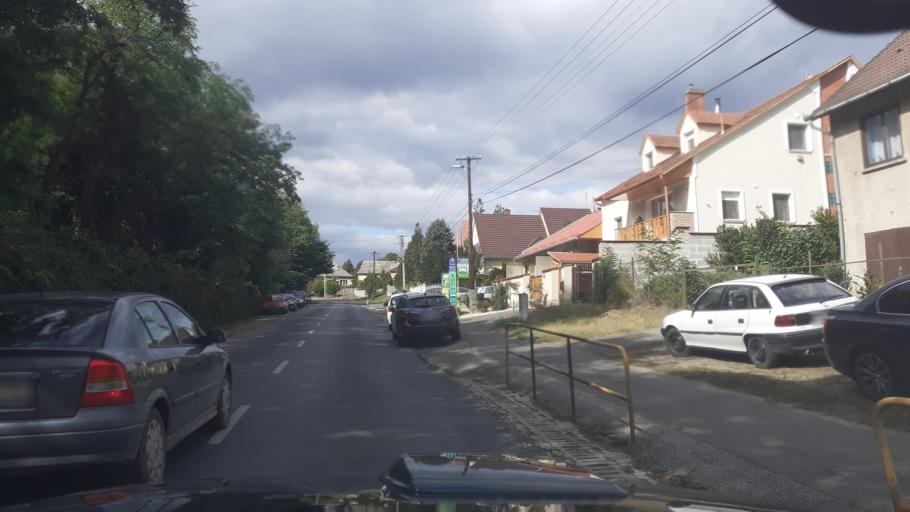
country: HU
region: Bacs-Kiskun
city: Solt
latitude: 46.8099
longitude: 18.9881
